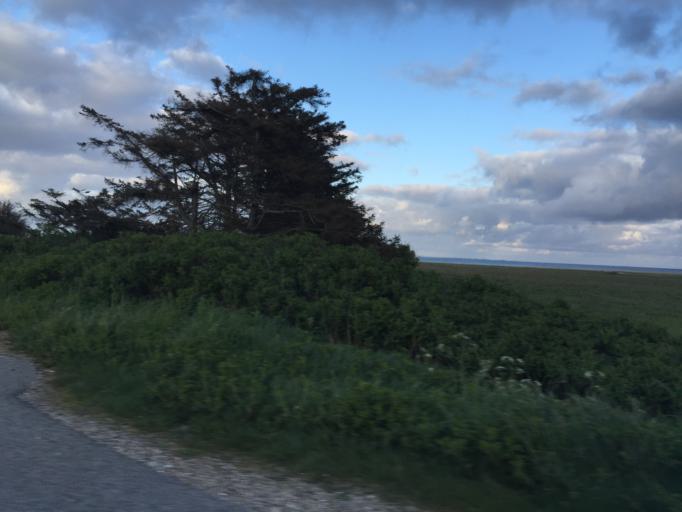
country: DK
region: Central Jutland
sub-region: Ringkobing-Skjern Kommune
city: Hvide Sande
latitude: 56.0447
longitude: 8.1191
